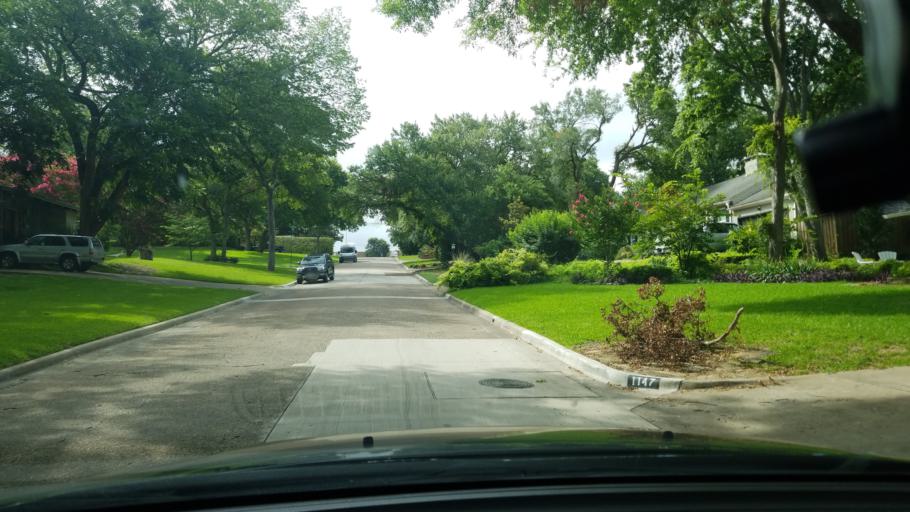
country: US
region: Texas
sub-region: Dallas County
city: Highland Park
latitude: 32.8268
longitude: -96.7136
